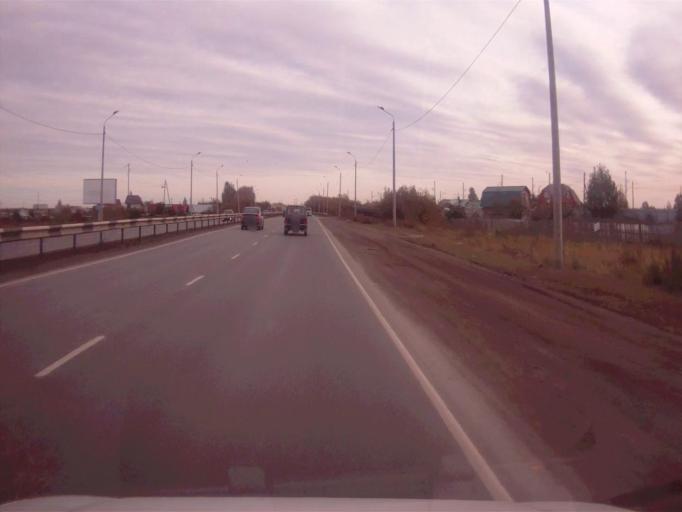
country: RU
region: Chelyabinsk
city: Novosineglazovskiy
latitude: 55.0449
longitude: 61.4212
